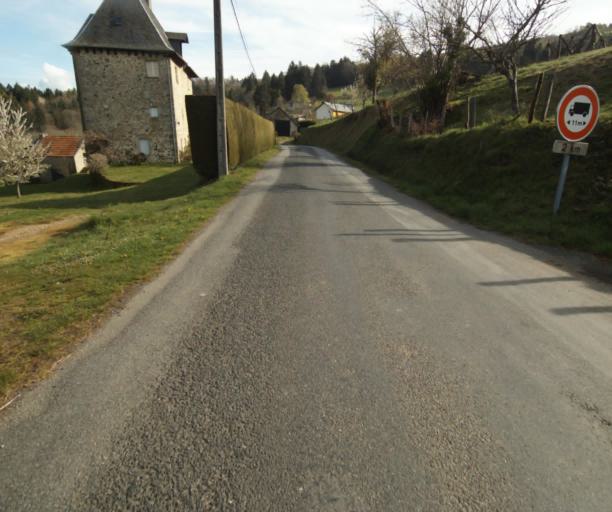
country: FR
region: Limousin
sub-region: Departement de la Correze
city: Naves
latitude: 45.3286
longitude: 1.8272
